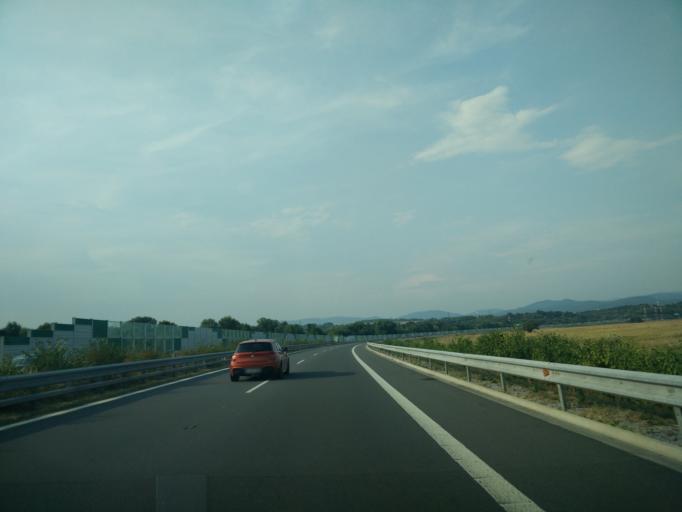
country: SK
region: Banskobystricky
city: Ziar nad Hronom
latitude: 48.5632
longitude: 18.8199
